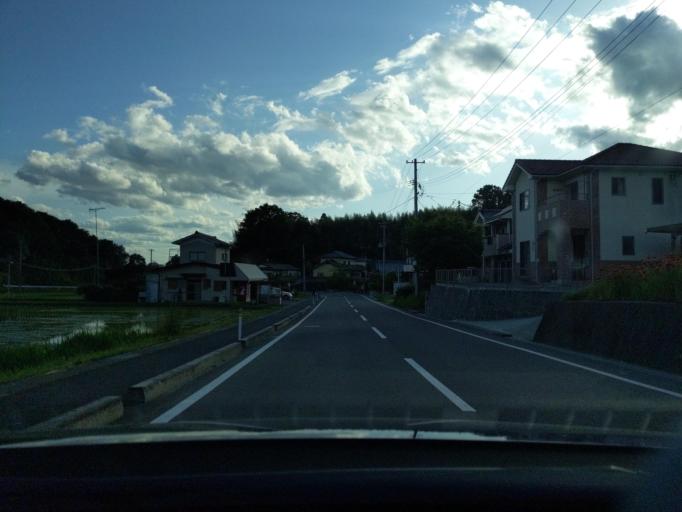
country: JP
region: Fukushima
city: Miharu
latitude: 37.4229
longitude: 140.4344
